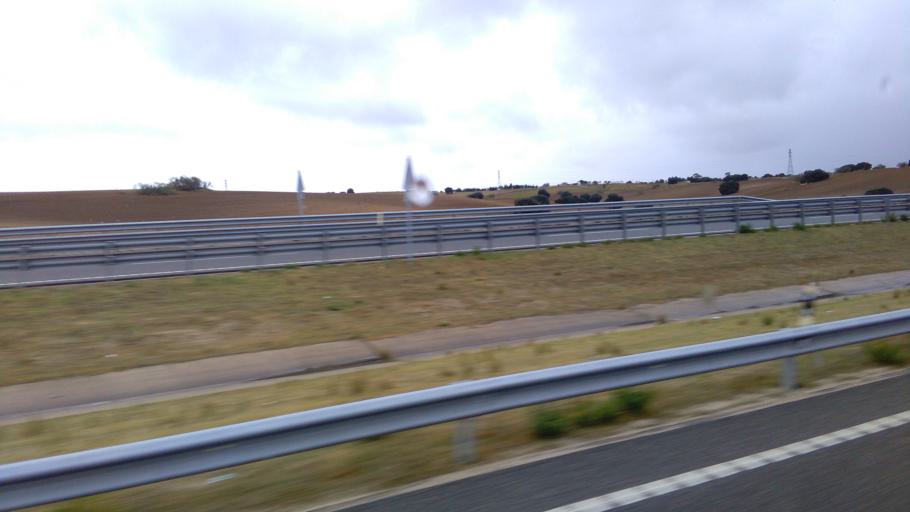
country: ES
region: Madrid
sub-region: Provincia de Madrid
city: Arroyomolinos
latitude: 40.2549
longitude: -3.9197
